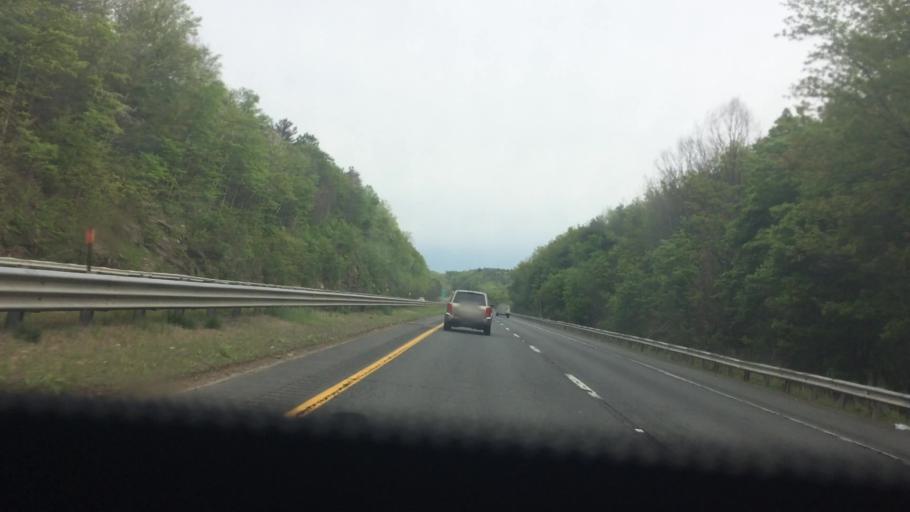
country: US
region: Massachusetts
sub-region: Worcester County
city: Fiskdale
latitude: 42.1430
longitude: -72.1385
